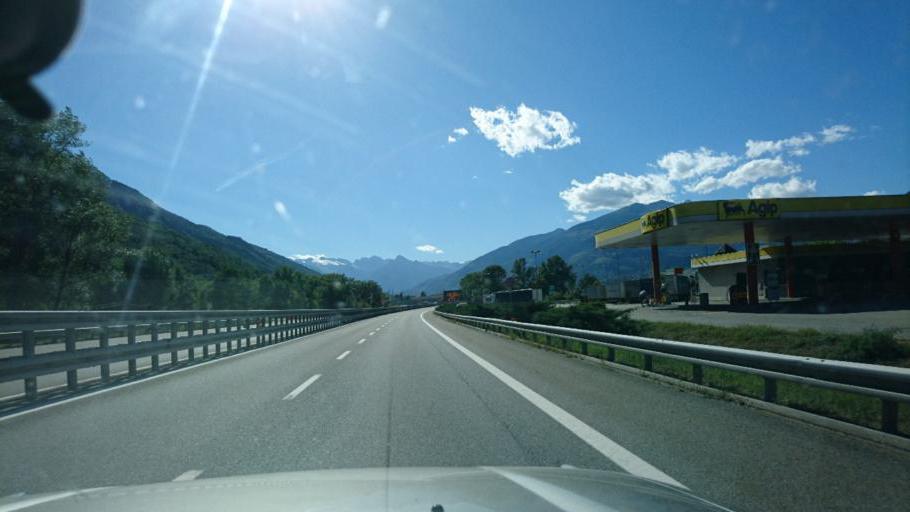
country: IT
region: Aosta Valley
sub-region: Valle d'Aosta
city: Quart
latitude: 45.7368
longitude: 7.4065
